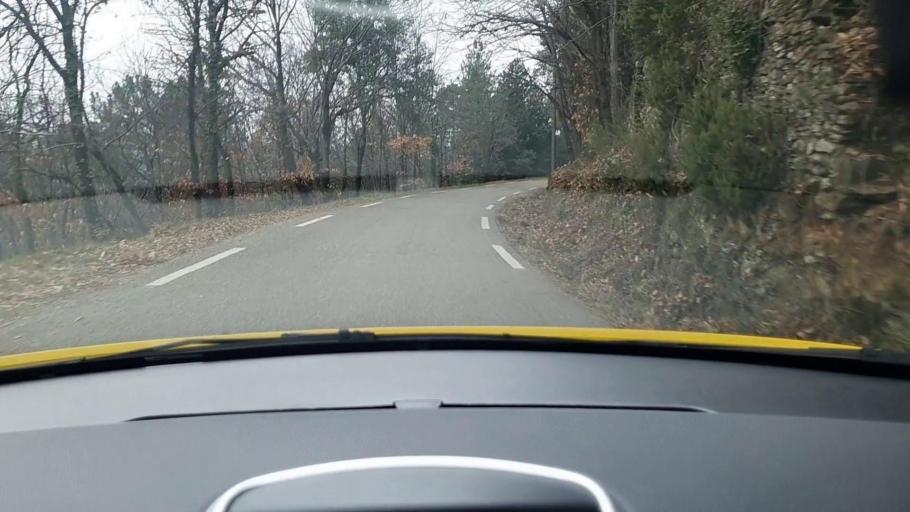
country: FR
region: Languedoc-Roussillon
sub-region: Departement du Gard
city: Besseges
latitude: 44.3440
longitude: 4.0406
